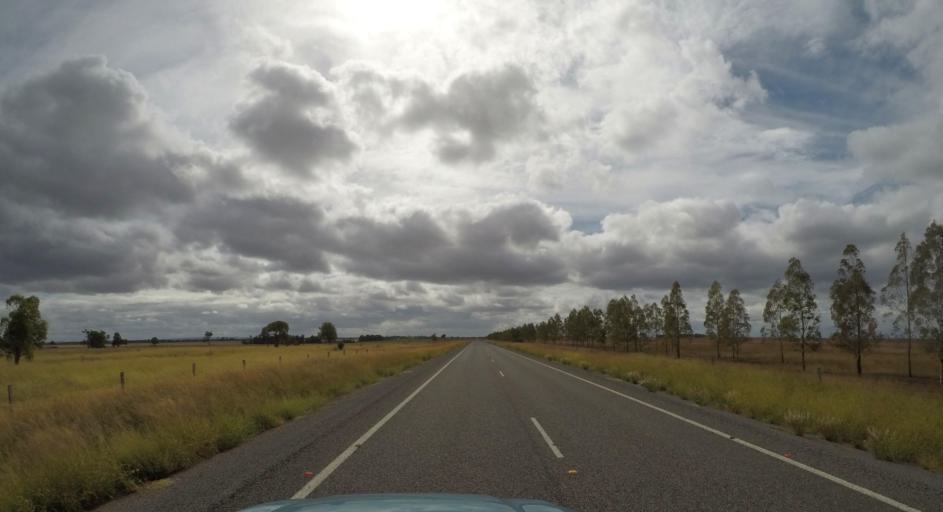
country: AU
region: Queensland
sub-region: South Burnett
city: Wondai
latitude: -26.3305
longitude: 151.2539
